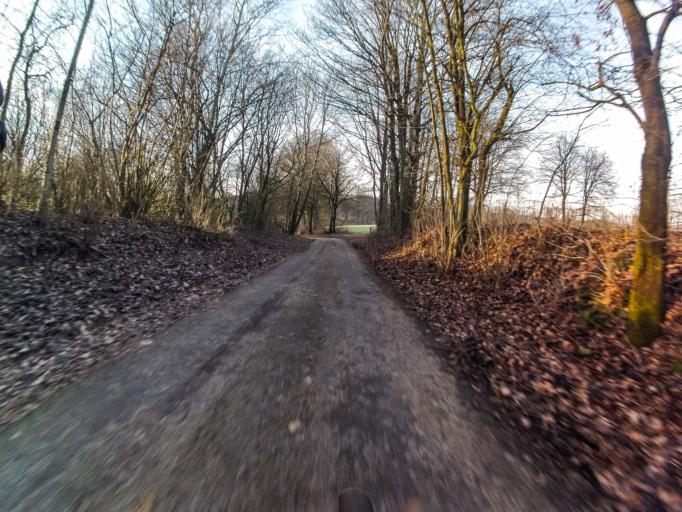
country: DE
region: North Rhine-Westphalia
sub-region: Regierungsbezirk Munster
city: Mettingen
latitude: 52.2867
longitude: 7.7993
